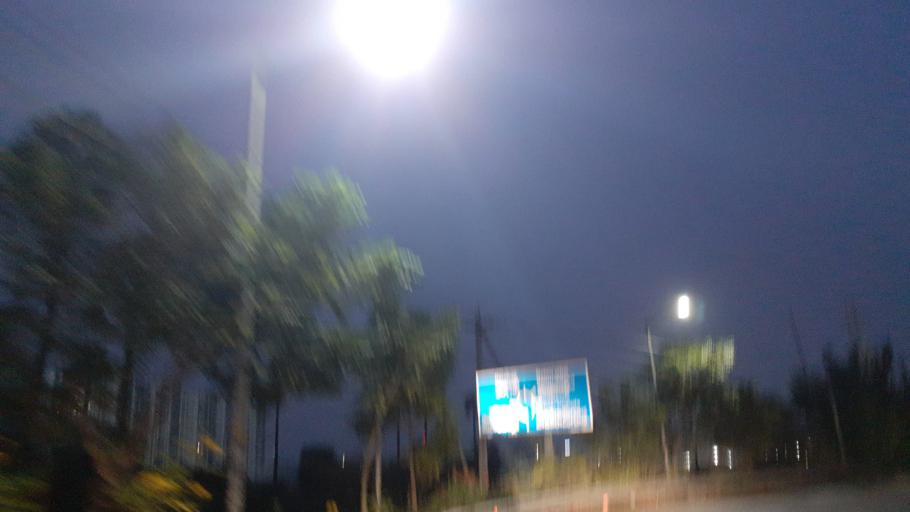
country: IN
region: Telangana
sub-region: Rangareddi
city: Kukatpalli
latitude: 17.4194
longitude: 78.3577
